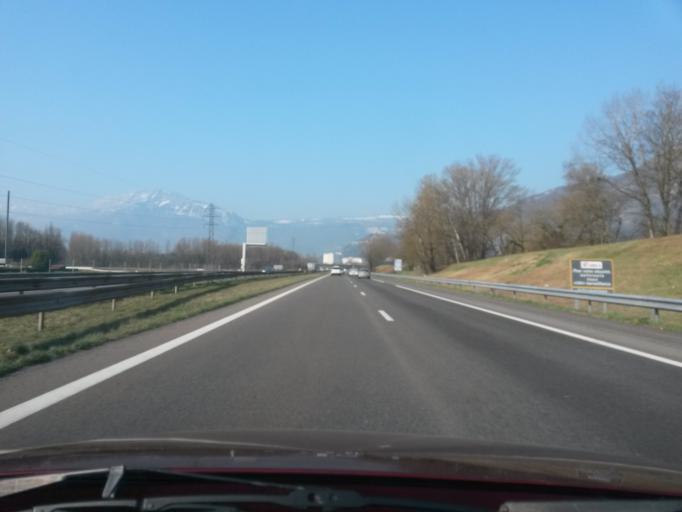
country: FR
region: Rhone-Alpes
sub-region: Departement de l'Isere
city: Corenc
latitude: 45.2034
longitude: 5.7766
